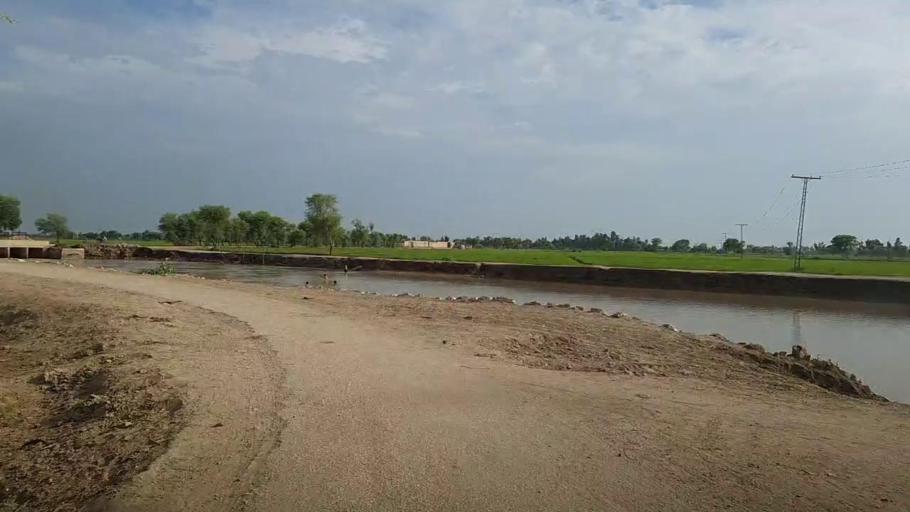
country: PK
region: Sindh
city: Thul
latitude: 28.2545
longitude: 68.8577
